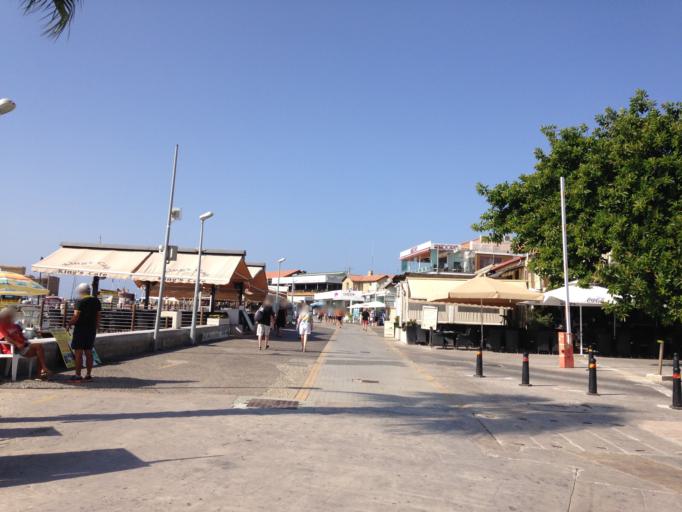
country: CY
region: Pafos
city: Paphos
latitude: 34.7558
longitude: 32.4089
